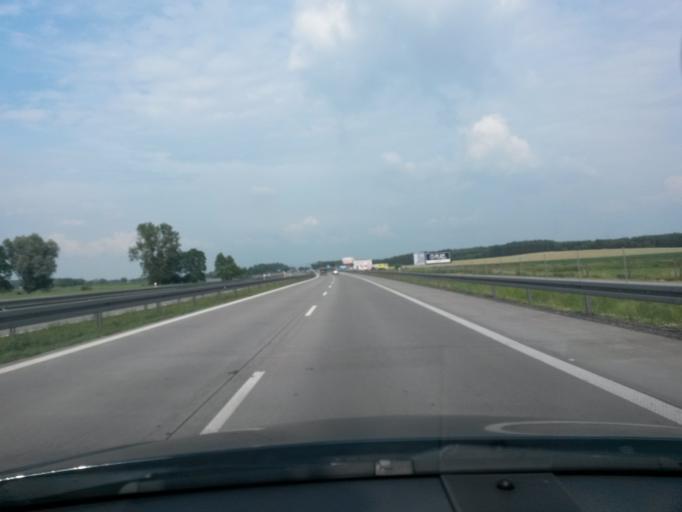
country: PL
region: Lodz Voivodeship
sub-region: Powiat piotrkowski
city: Wolborz
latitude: 51.4992
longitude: 19.8585
